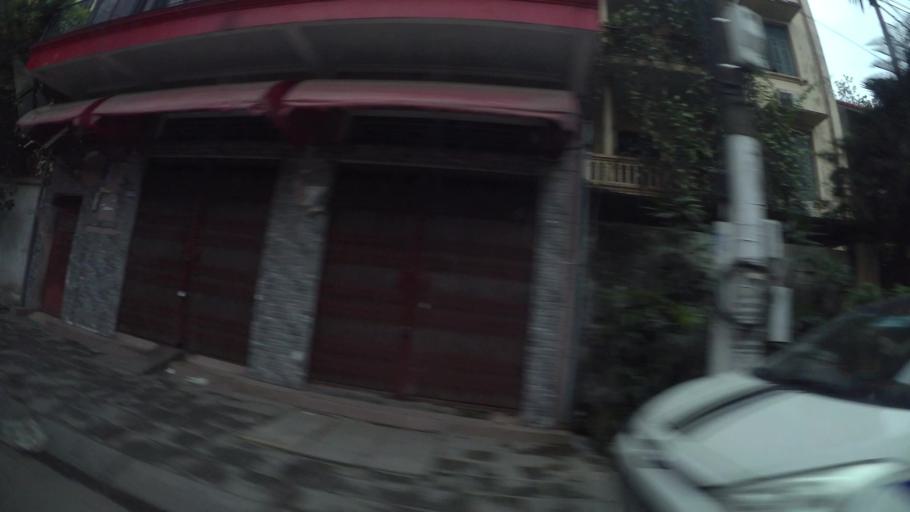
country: VN
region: Ha Noi
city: Hoan Kiem
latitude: 21.0204
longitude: 105.8631
